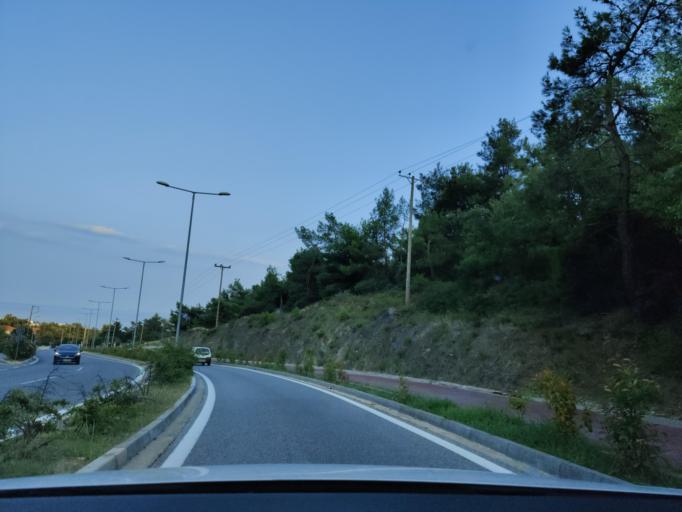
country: GR
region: East Macedonia and Thrace
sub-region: Nomos Kavalas
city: Kavala
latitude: 40.9385
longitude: 24.3806
